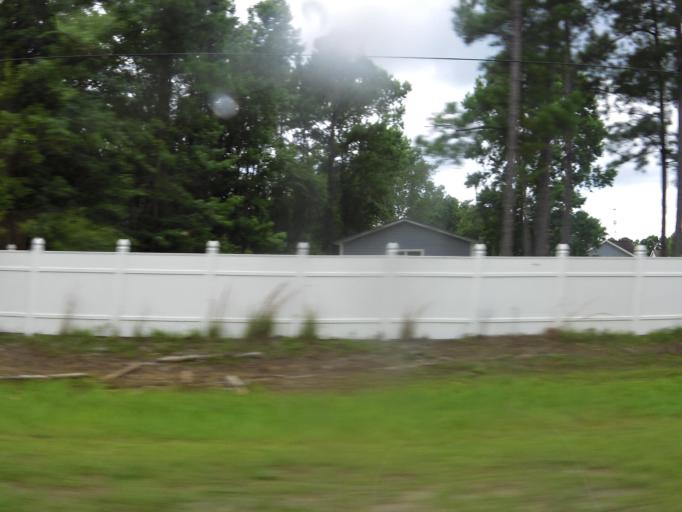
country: US
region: Georgia
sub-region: Camden County
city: Kingsland
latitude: 30.7733
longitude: -81.6504
